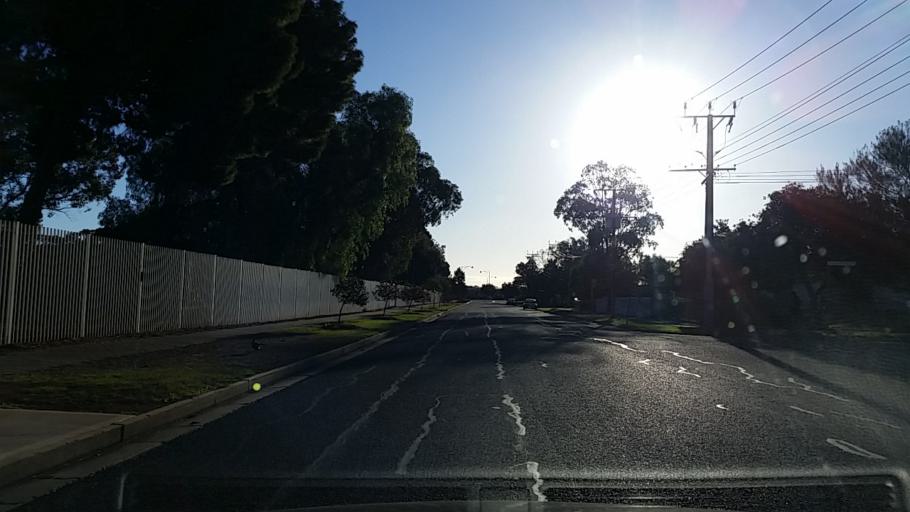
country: AU
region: South Australia
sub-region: Playford
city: Smithfield
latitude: -34.6856
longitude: 138.6660
